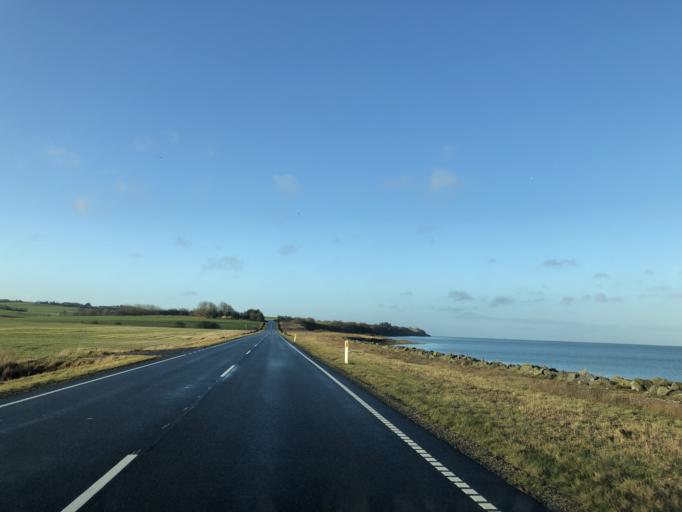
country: DK
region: Central Jutland
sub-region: Struer Kommune
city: Struer
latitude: 56.5578
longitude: 8.4673
